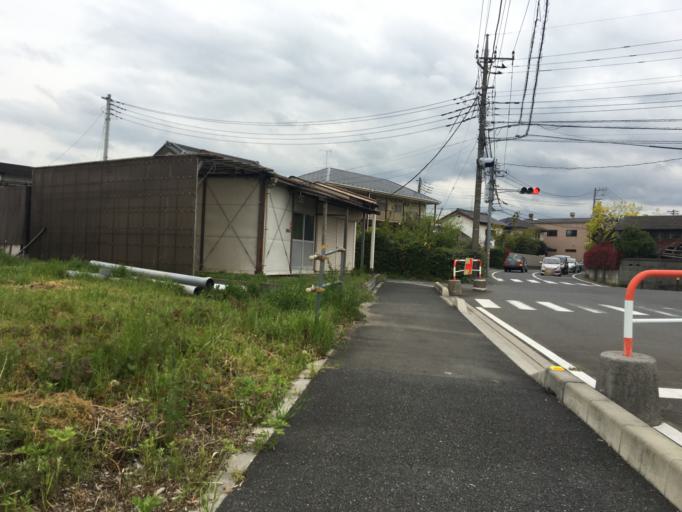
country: JP
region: Saitama
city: Oi
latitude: 35.8531
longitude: 139.5537
